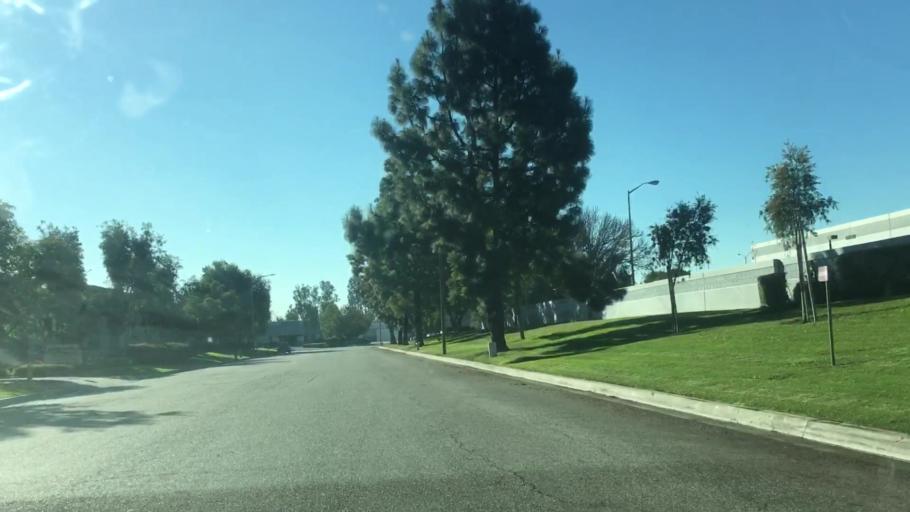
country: US
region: California
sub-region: Los Angeles County
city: Cerritos
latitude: 33.8839
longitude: -118.0488
